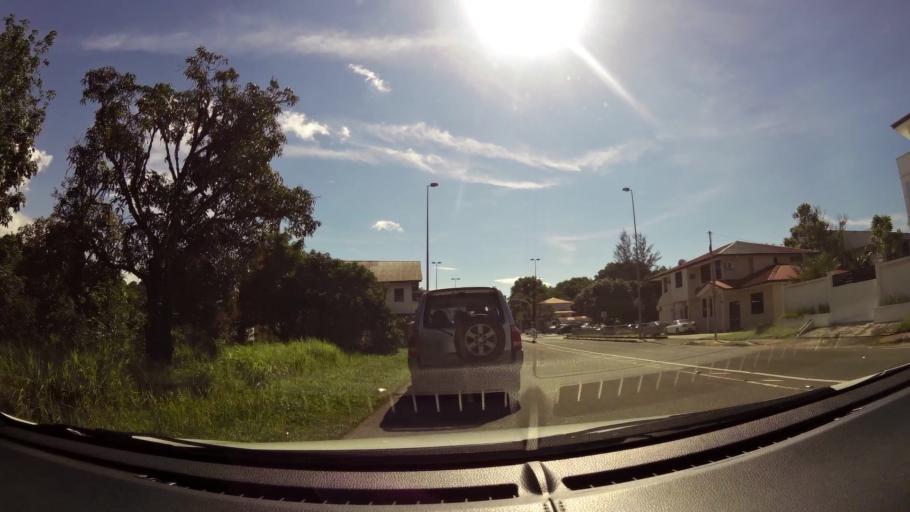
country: BN
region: Brunei and Muara
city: Bandar Seri Begawan
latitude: 4.9644
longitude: 114.9473
